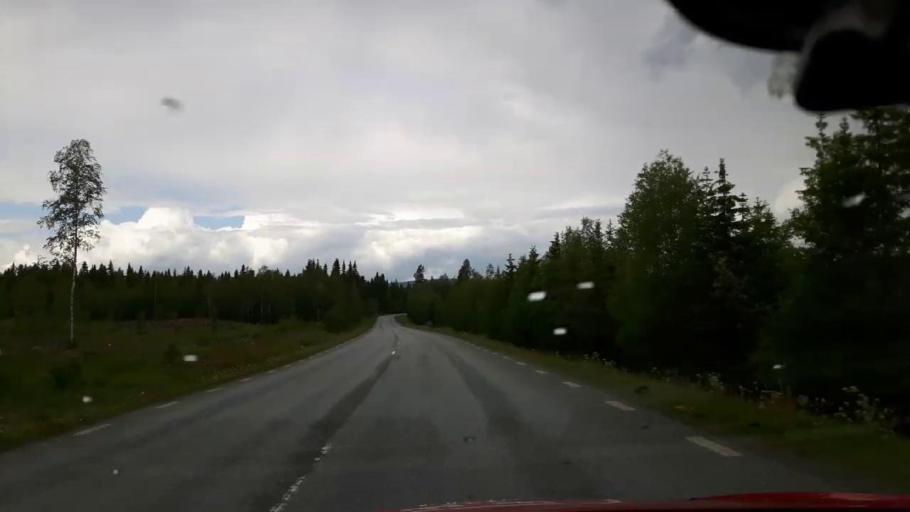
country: SE
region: Jaemtland
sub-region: Krokoms Kommun
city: Krokom
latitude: 63.4262
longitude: 14.2148
